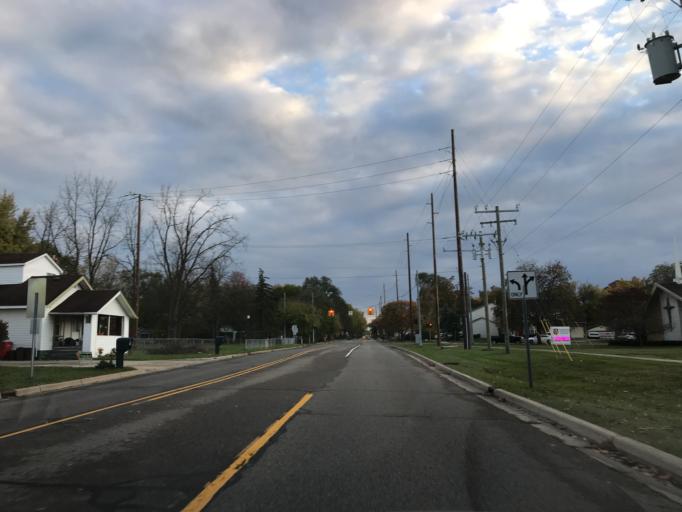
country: US
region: Michigan
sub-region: Oakland County
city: Farmington
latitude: 42.4508
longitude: -83.3173
